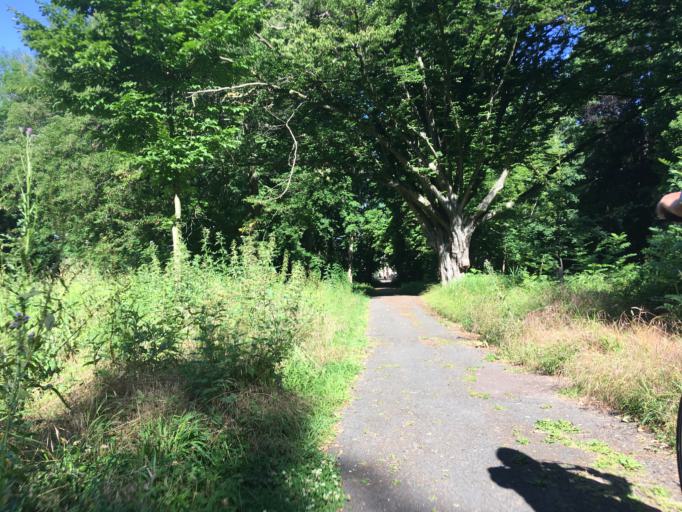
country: DE
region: Saxony-Anhalt
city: Koethen
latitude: 51.7603
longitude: 11.9396
